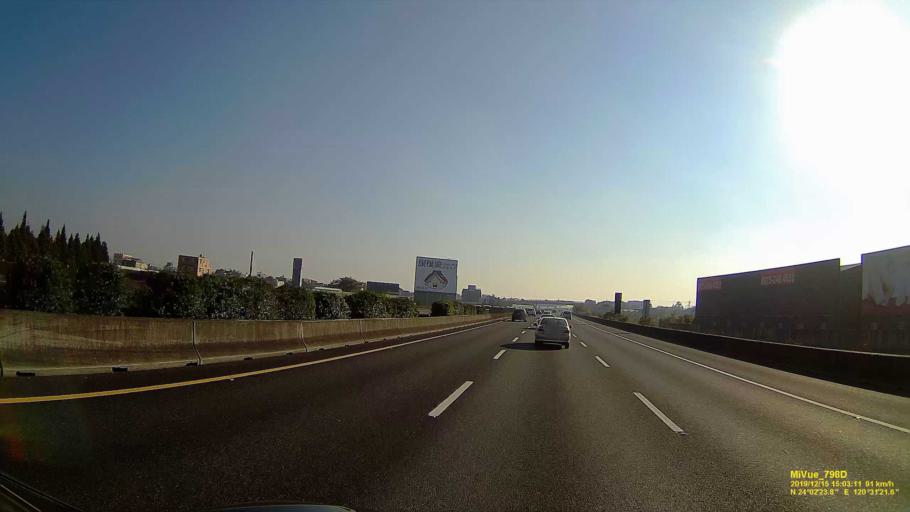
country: TW
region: Taiwan
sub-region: Changhua
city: Chang-hua
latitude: 24.0391
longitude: 120.5229
